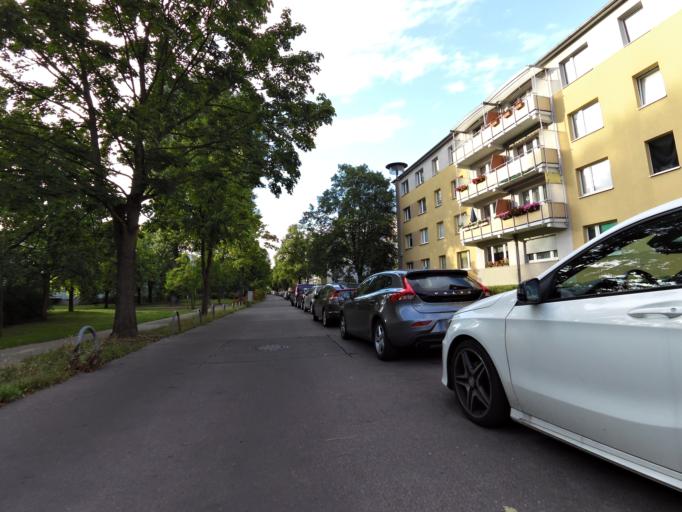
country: DE
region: Berlin
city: Baumschulenweg
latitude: 52.4670
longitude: 13.4814
